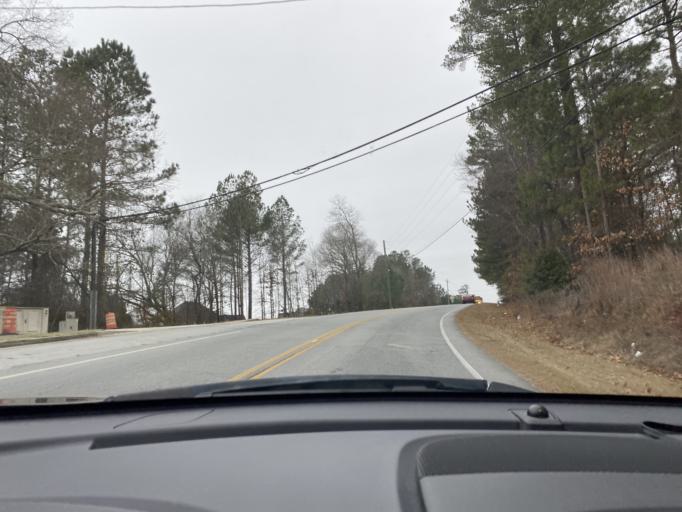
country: US
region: Georgia
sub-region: Gwinnett County
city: Dacula
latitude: 33.9143
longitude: -83.8778
